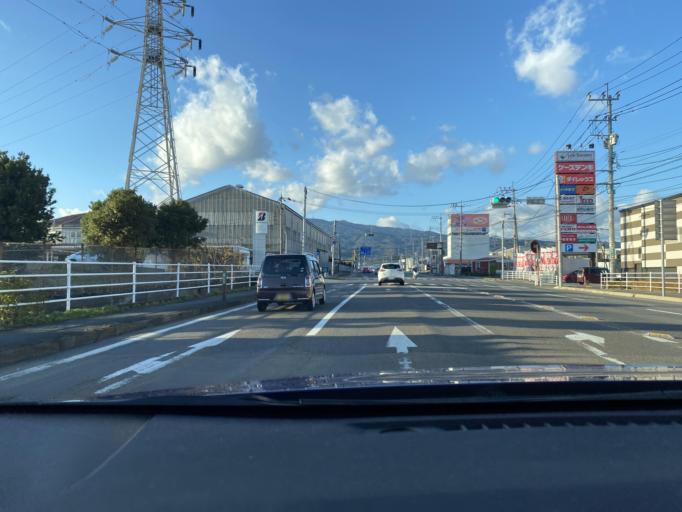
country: JP
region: Saga Prefecture
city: Tosu
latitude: 33.3635
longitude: 130.5035
